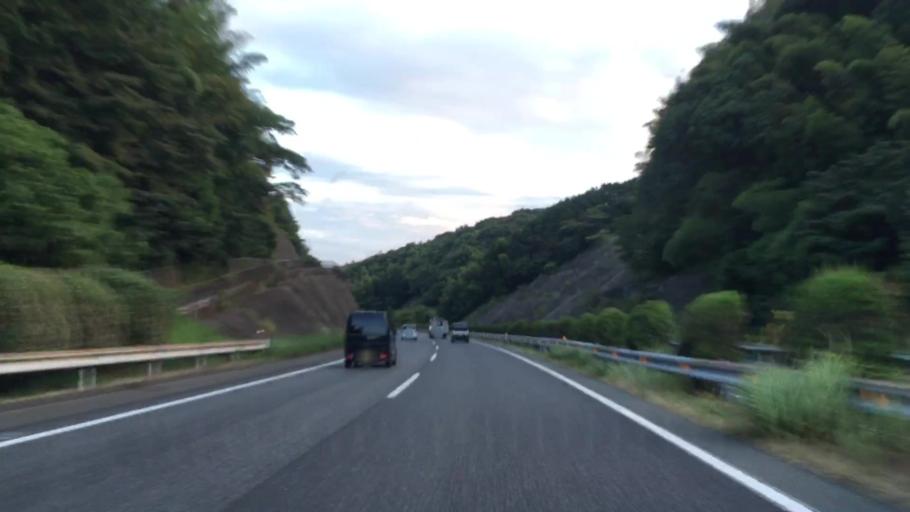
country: JP
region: Yamaguchi
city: Shimonoseki
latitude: 33.9043
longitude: 130.9716
